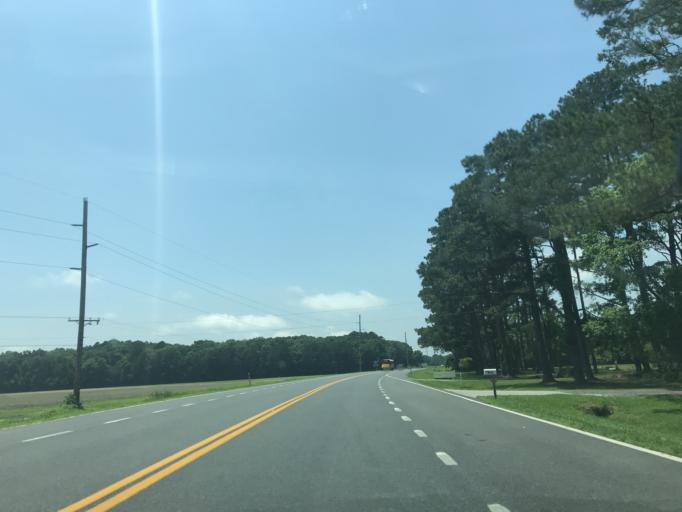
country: US
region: Maryland
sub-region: Dorchester County
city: Hurlock
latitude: 38.5914
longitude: -75.9273
